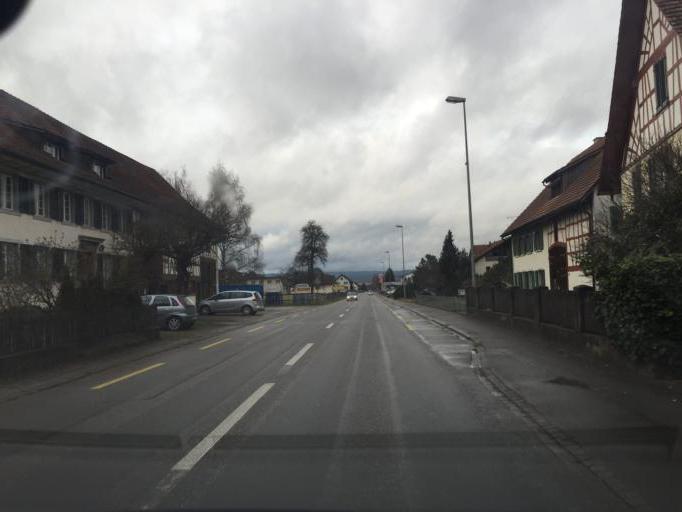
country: DE
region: Baden-Wuerttemberg
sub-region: Freiburg Region
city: Busingen
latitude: 47.6635
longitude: 8.7022
